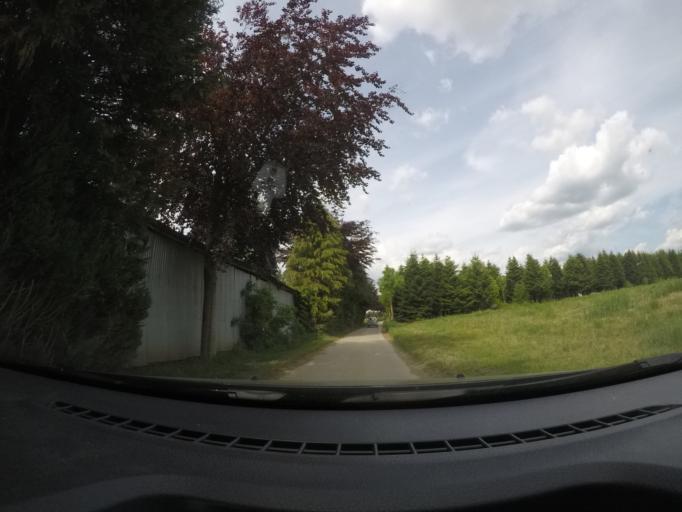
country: BE
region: Wallonia
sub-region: Province du Luxembourg
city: Leglise
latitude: 49.8108
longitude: 5.5610
